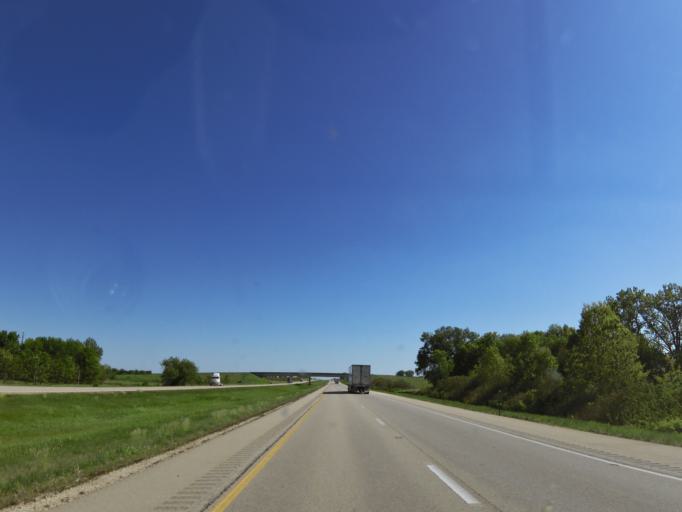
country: US
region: Illinois
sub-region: Ogle County
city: Rochelle
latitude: 41.7929
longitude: -89.0103
